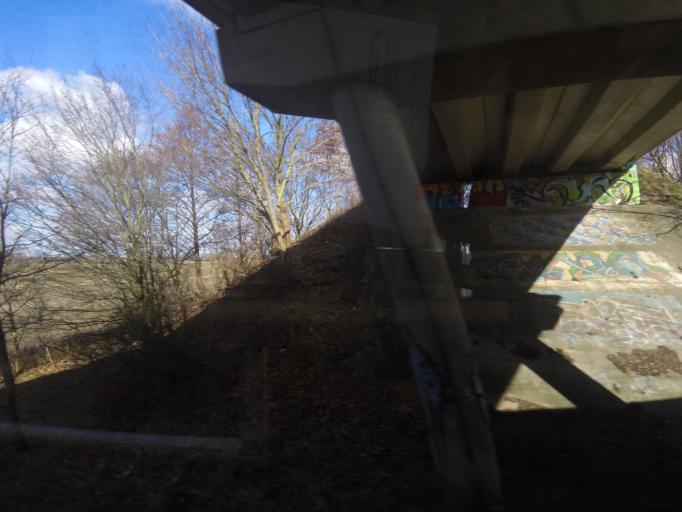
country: DE
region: Lower Saxony
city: Oyten
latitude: 53.0841
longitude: 8.9708
